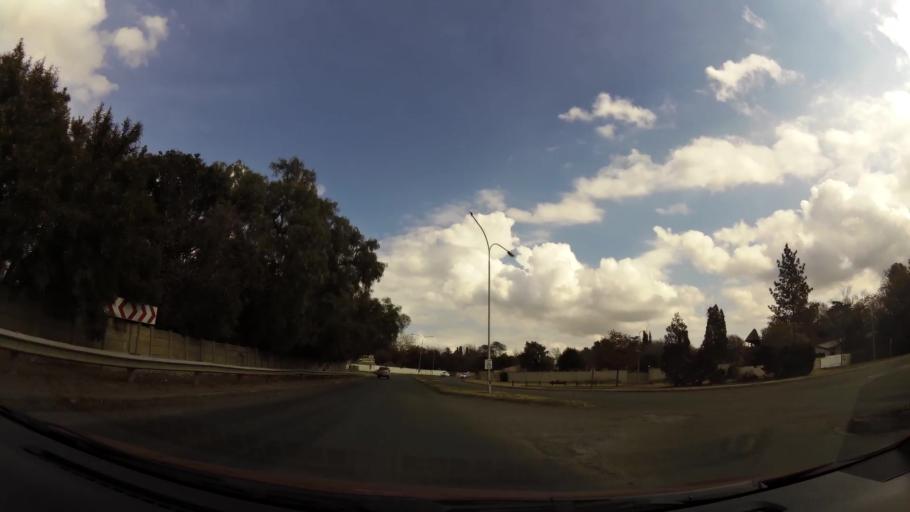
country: ZA
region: Gauteng
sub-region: Sedibeng District Municipality
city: Vanderbijlpark
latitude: -26.7317
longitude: 27.8322
